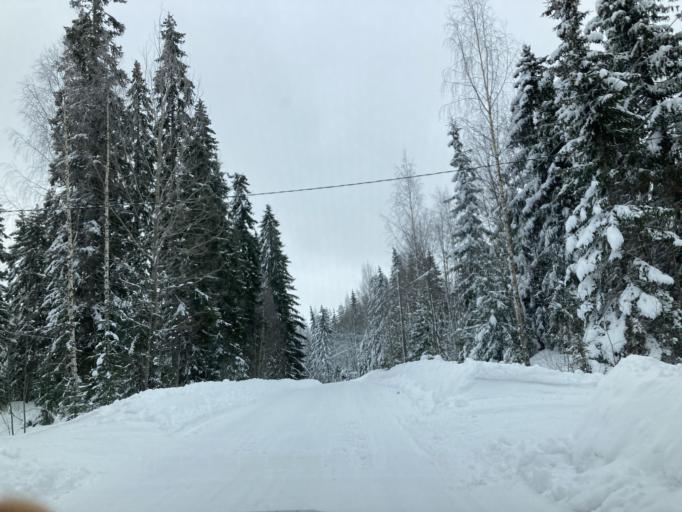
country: FI
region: Central Finland
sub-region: Jaemsae
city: Jaemsae
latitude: 61.8782
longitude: 25.3202
